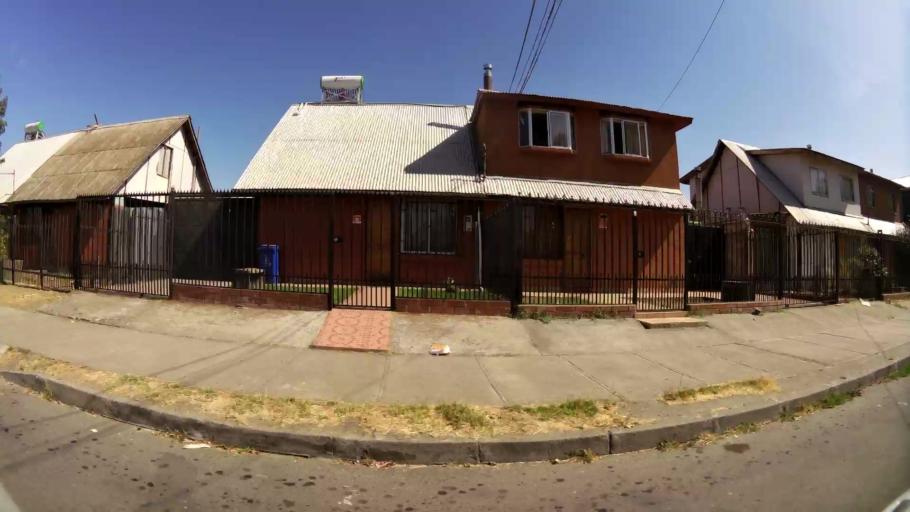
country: CL
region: Maule
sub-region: Provincia de Talca
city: Talca
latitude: -35.4102
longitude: -71.6356
